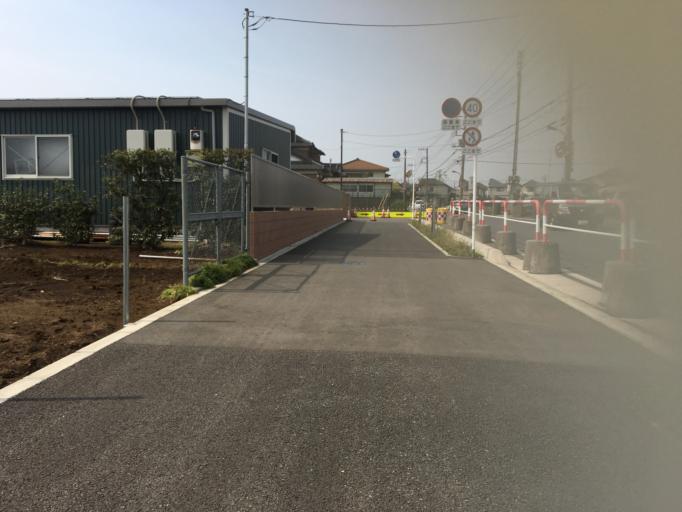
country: JP
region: Saitama
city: Shiki
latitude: 35.8048
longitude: 139.5457
